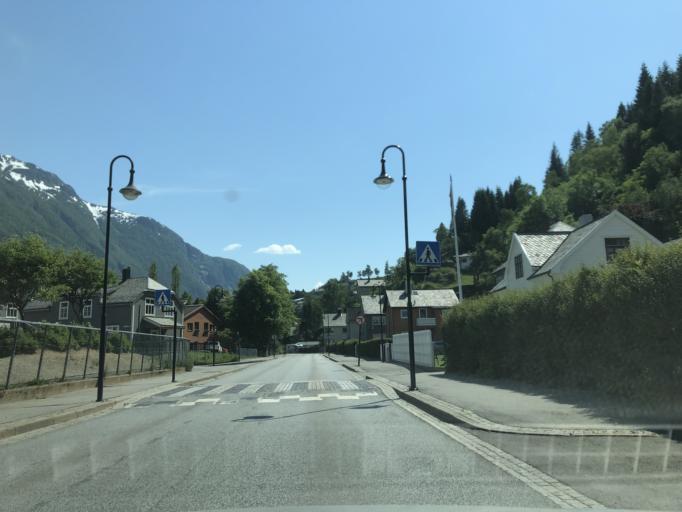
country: NO
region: Hordaland
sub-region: Odda
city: Odda
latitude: 60.0686
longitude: 6.5416
